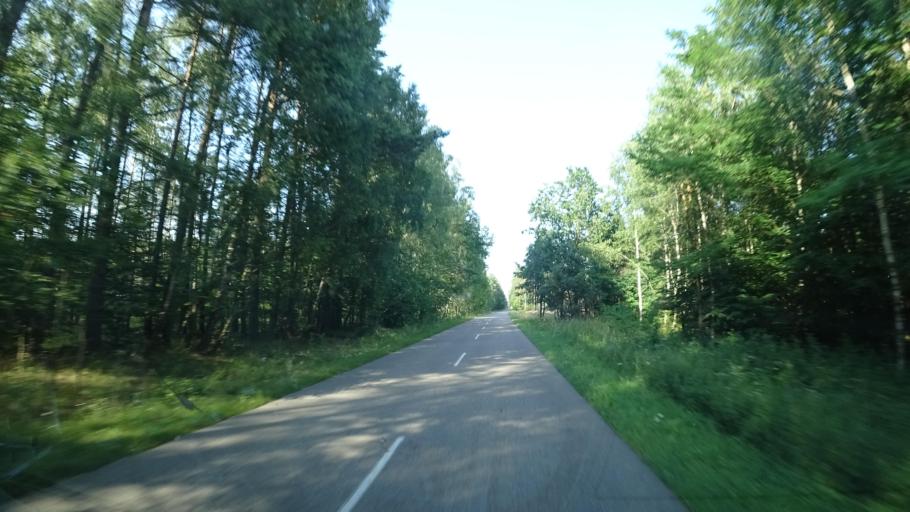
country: PL
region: Pomeranian Voivodeship
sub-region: Powiat czluchowski
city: Rzeczenica
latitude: 53.7726
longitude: 17.1516
